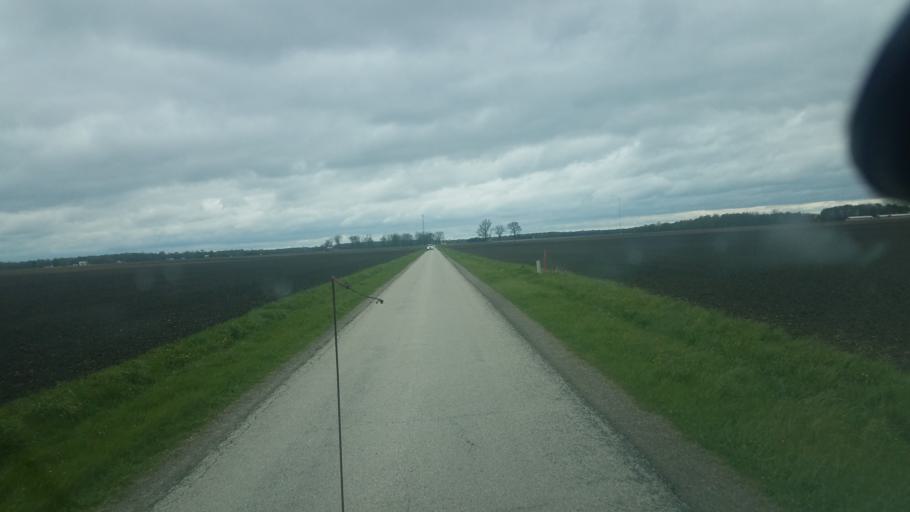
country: US
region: Ohio
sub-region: Crawford County
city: Bucyrus
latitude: 40.7256
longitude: -83.0734
